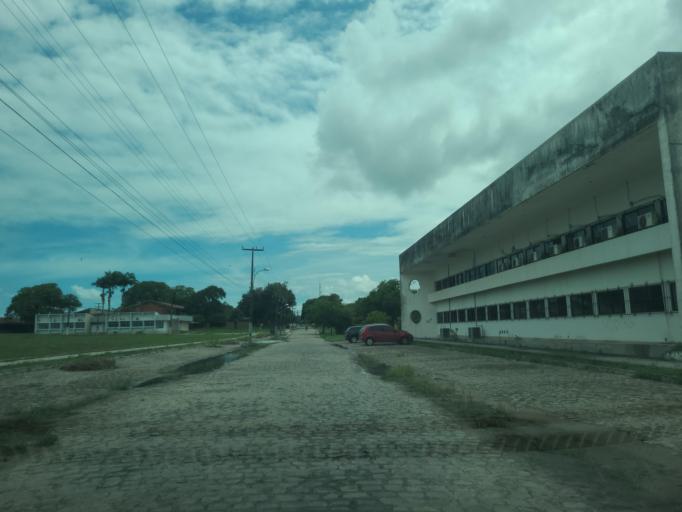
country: BR
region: Alagoas
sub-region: Satuba
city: Satuba
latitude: -9.5551
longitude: -35.7738
